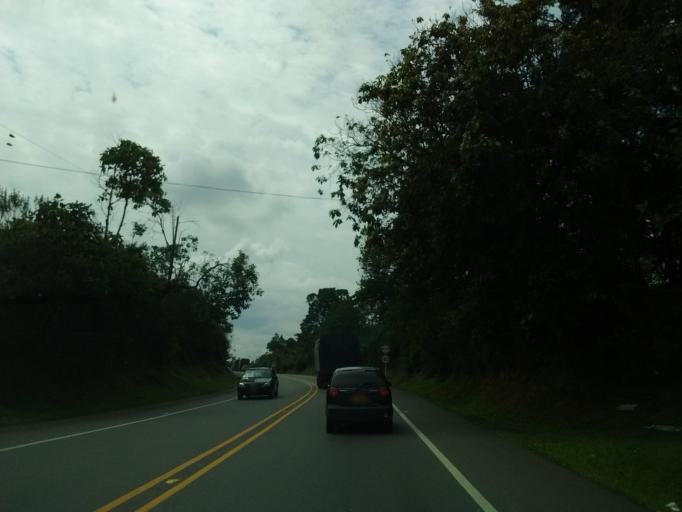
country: CO
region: Cauca
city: Morales
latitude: 2.7608
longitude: -76.5539
